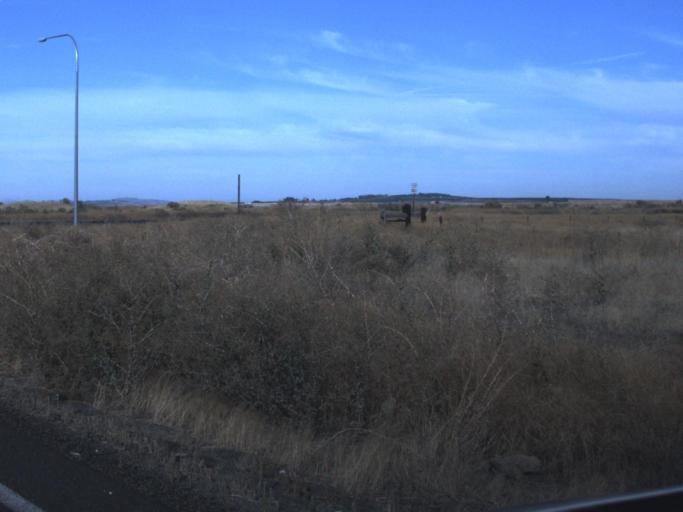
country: US
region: Washington
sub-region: Franklin County
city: Connell
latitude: 46.6650
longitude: -119.0058
